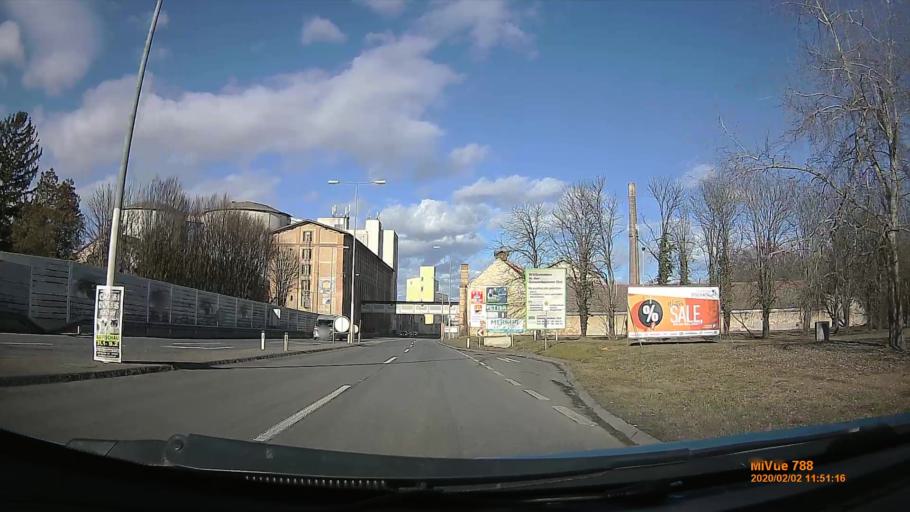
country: AT
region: Burgenland
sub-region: Eisenstadt-Umgebung
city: Zagersdorf
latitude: 47.7684
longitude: 16.5316
